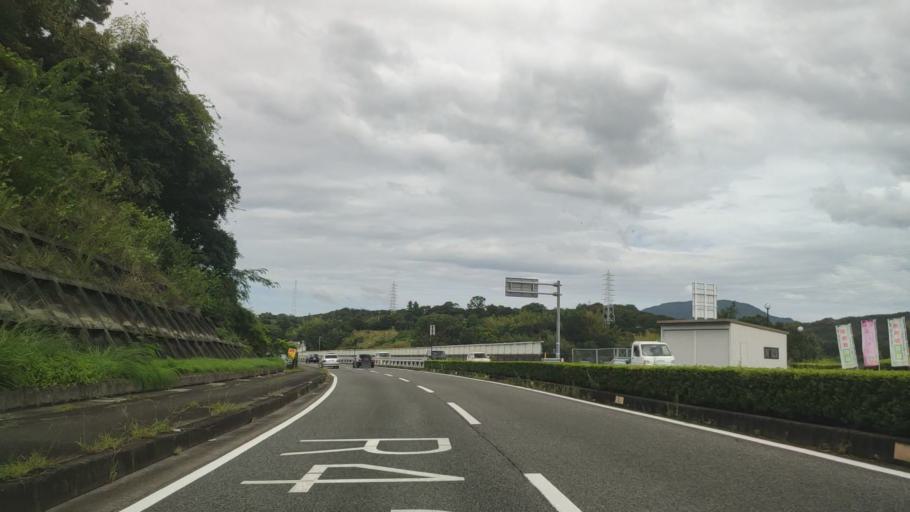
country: JP
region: Wakayama
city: Tanabe
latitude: 33.7169
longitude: 135.4079
